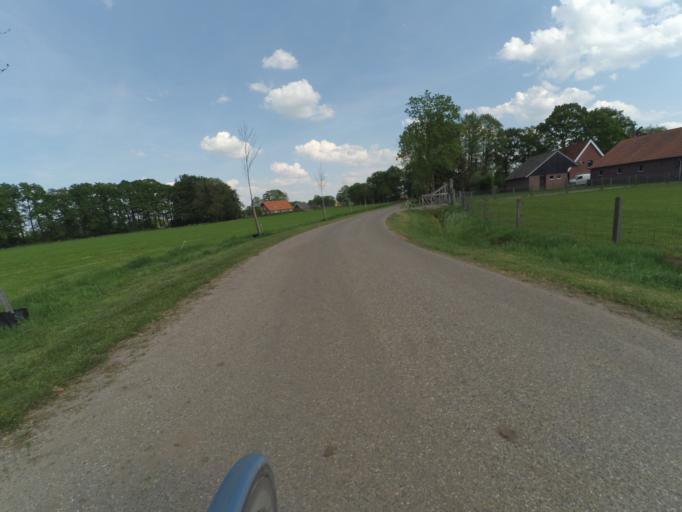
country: NL
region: Overijssel
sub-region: Gemeente Tubbergen
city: Tubbergen
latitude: 52.3624
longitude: 6.8202
